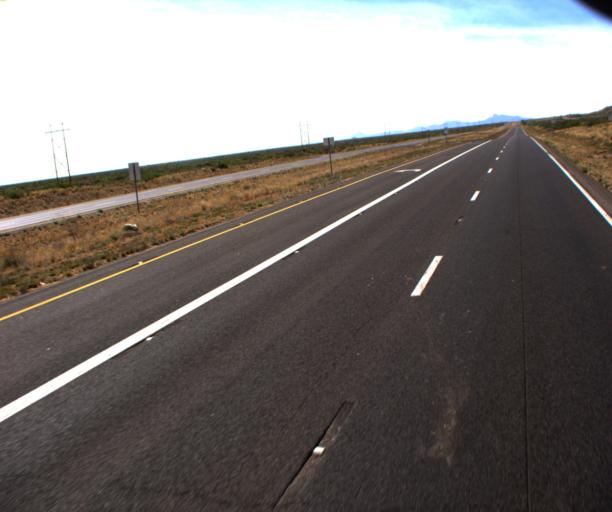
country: US
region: Arizona
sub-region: Graham County
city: Swift Trail Junction
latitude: 32.5573
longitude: -109.6789
